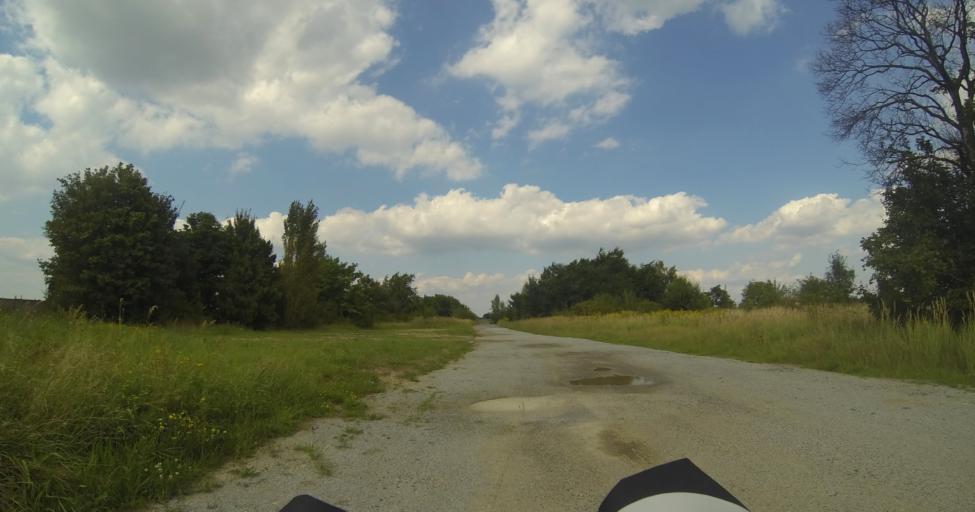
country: DE
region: Saxony
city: Grossenhain
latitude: 51.3102
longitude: 13.5384
